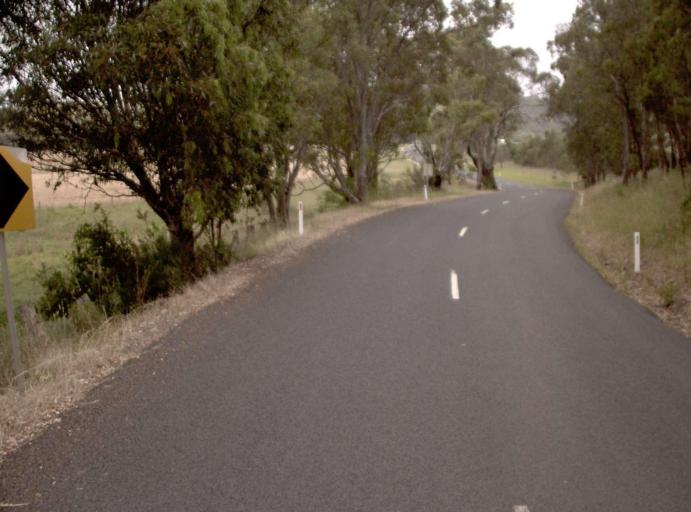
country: AU
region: Victoria
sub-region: Wellington
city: Heyfield
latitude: -37.8955
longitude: 146.7239
